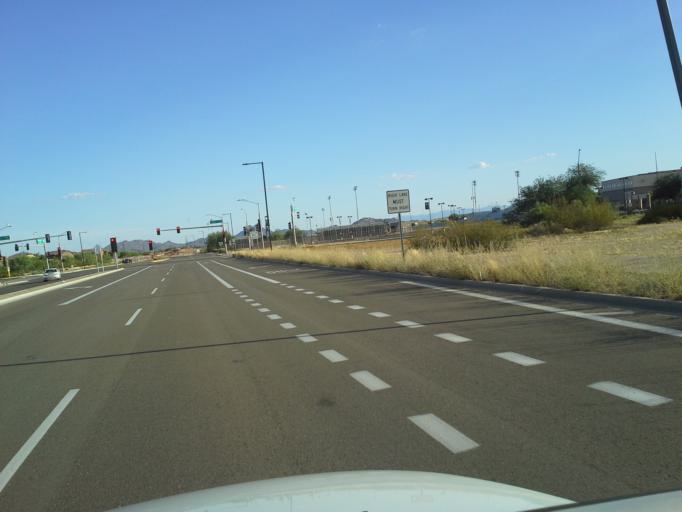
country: US
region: Arizona
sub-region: Maricopa County
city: Cave Creek
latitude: 33.6820
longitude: -112.0052
